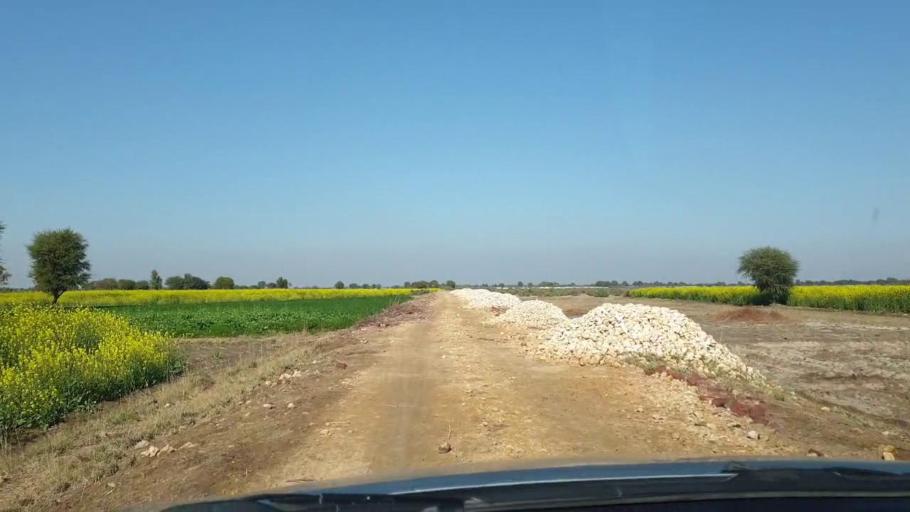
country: PK
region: Sindh
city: Jhol
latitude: 25.9233
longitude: 68.9443
